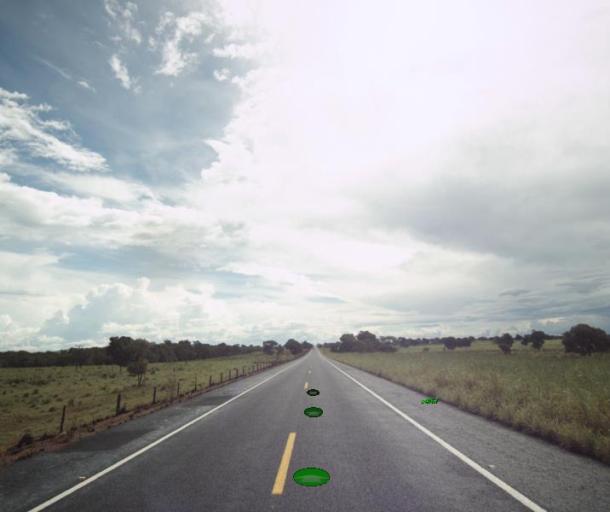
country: BR
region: Goias
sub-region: Sao Miguel Do Araguaia
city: Sao Miguel do Araguaia
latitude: -13.2918
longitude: -50.4076
